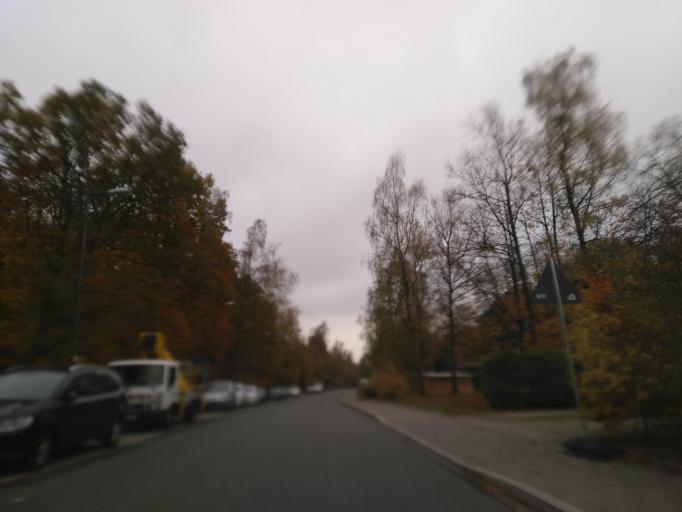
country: DE
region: Bavaria
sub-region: Upper Bavaria
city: Unterhaching
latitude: 48.0926
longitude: 11.6044
